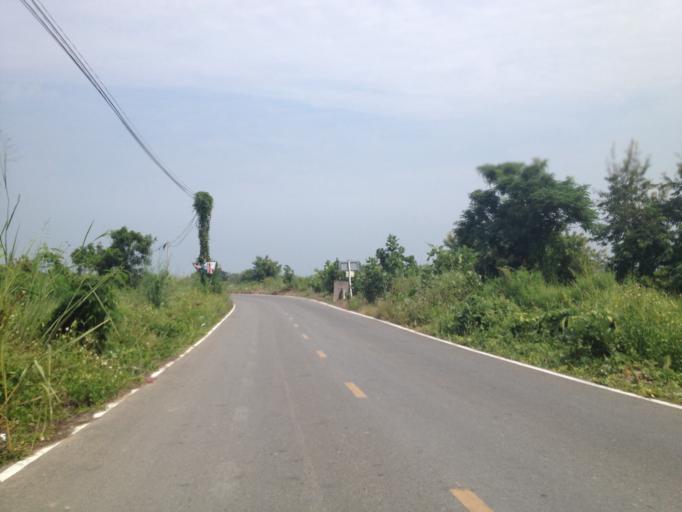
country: TH
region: Chiang Mai
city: San Pa Tong
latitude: 18.6520
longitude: 98.8691
